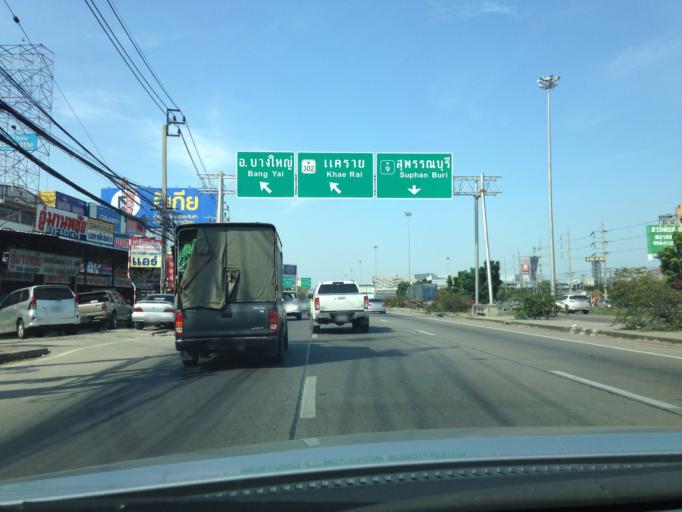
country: TH
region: Nonthaburi
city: Bang Bua Thong
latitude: 13.8692
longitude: 100.4101
